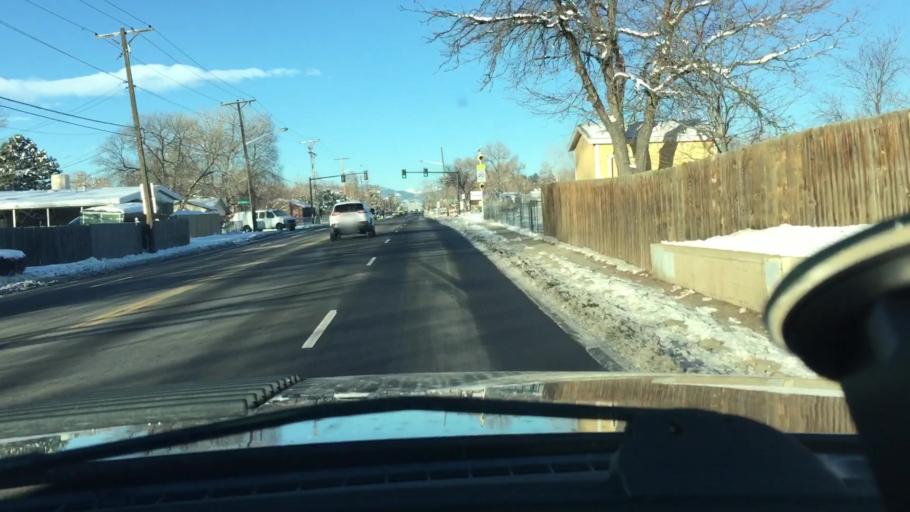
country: US
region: Colorado
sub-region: Adams County
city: Westminster
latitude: 39.8418
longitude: -105.0276
